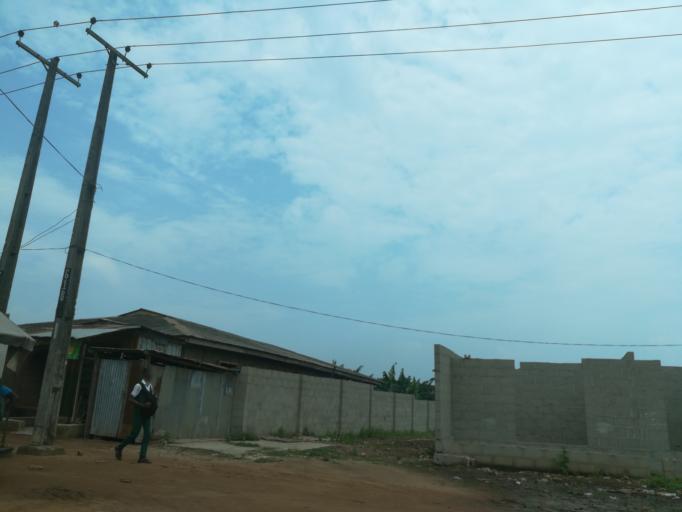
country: NG
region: Lagos
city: Ikorodu
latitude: 6.5738
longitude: 3.5922
